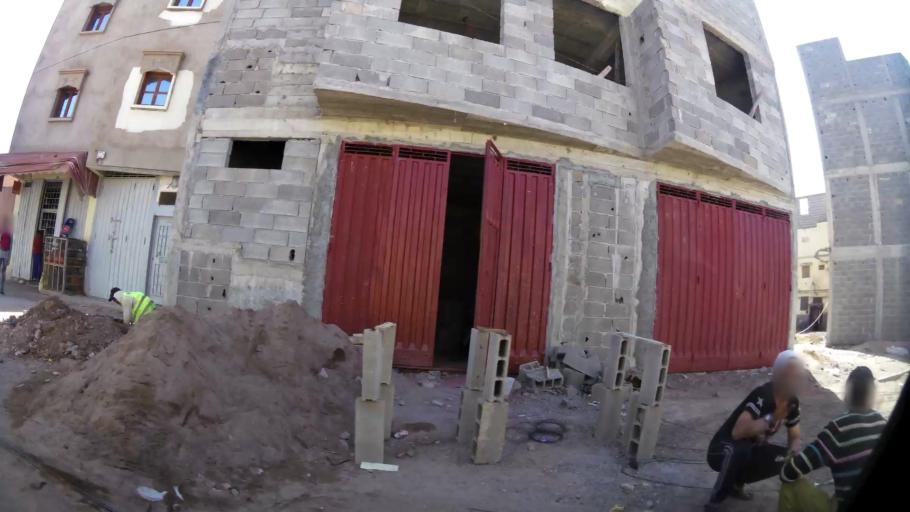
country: MA
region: Souss-Massa-Draa
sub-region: Inezgane-Ait Mellou
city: Inezgane
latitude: 30.3520
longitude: -9.5570
